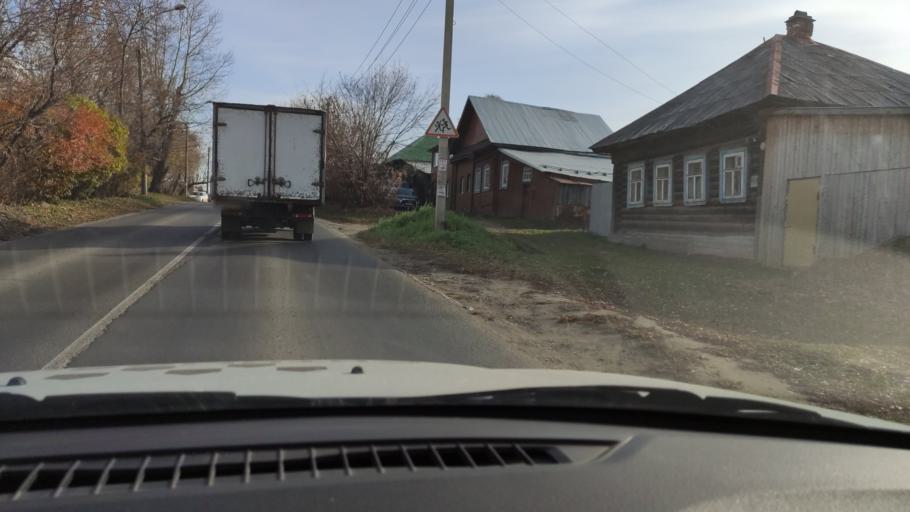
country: RU
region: Perm
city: Perm
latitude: 58.0370
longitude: 56.3320
